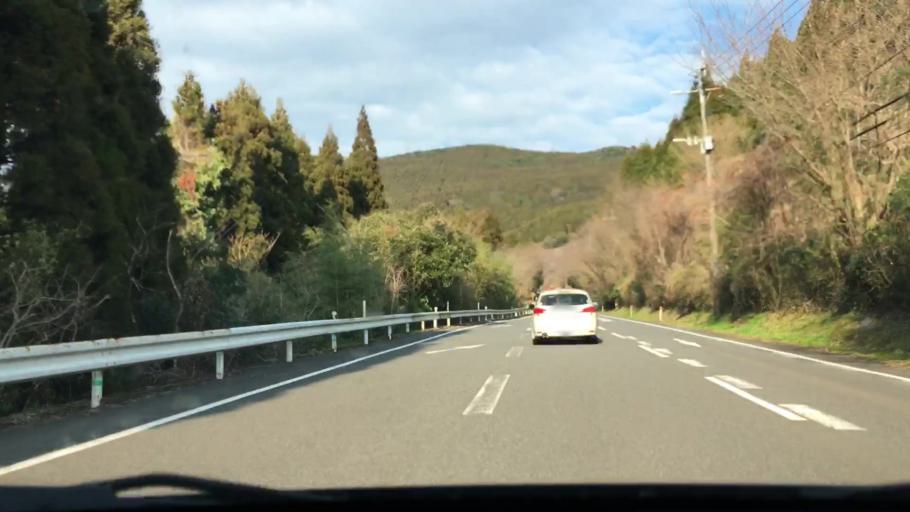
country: JP
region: Miyazaki
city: Miyazaki-shi
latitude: 31.7725
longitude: 131.3300
